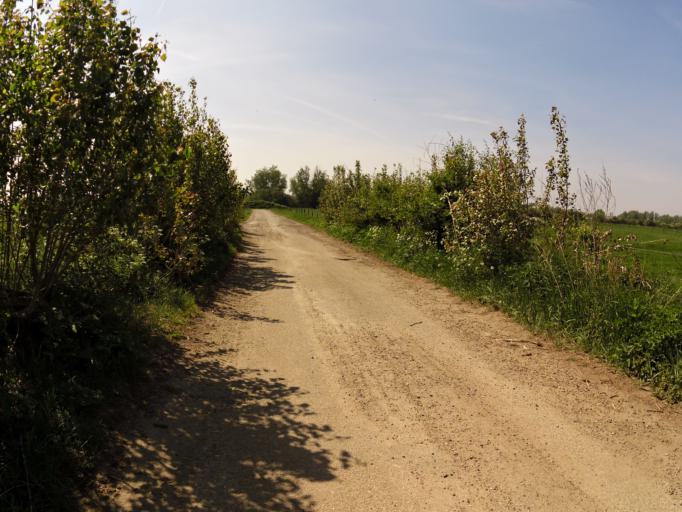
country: NL
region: Gelderland
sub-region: Gemeente Neerijnen
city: Neerijnen
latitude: 51.8135
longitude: 5.3056
